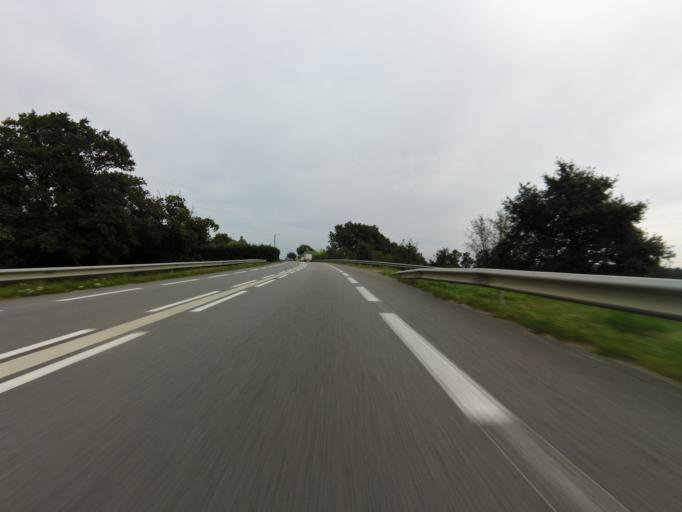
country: FR
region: Brittany
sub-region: Departement du Morbihan
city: Plescop
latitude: 47.6986
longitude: -2.7804
